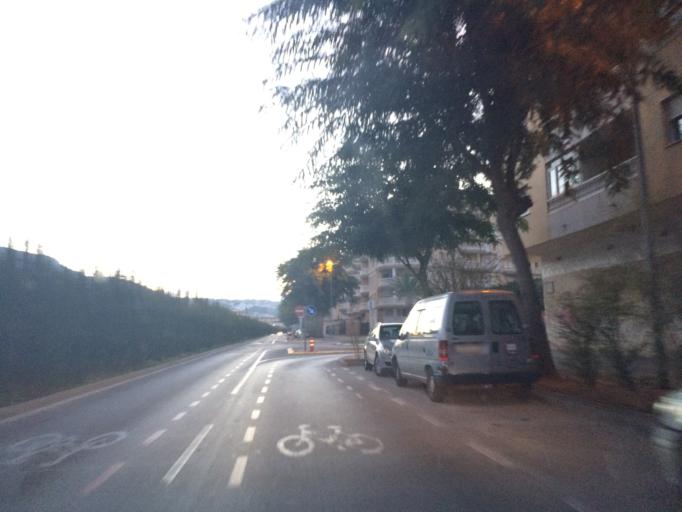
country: ES
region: Valencia
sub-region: Provincia de Alicante
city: Denia
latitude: 38.8346
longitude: 0.1070
